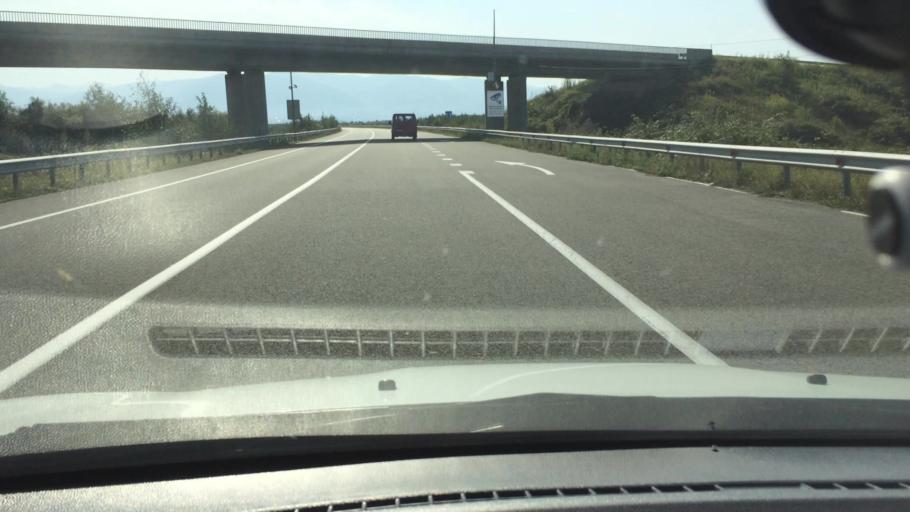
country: GE
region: Guria
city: Urek'i
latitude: 41.9183
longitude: 41.7758
